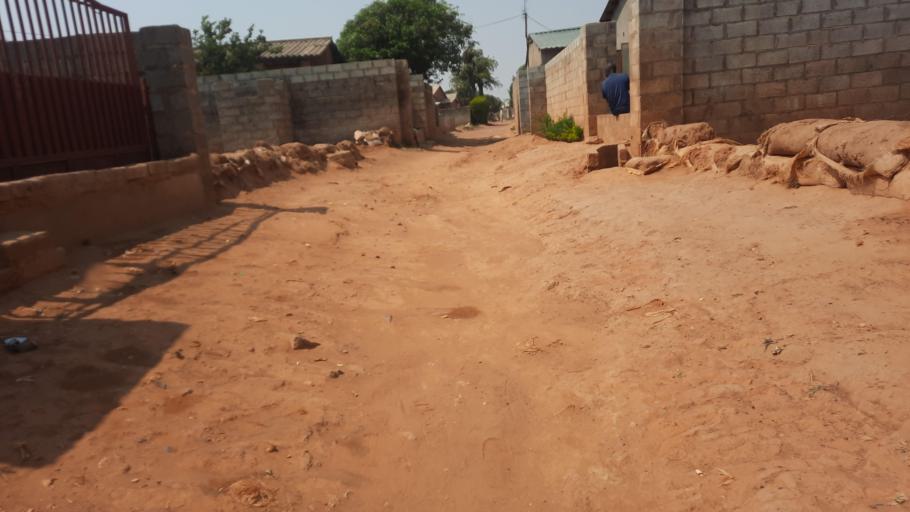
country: ZM
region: Lusaka
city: Lusaka
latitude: -15.3927
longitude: 28.3823
